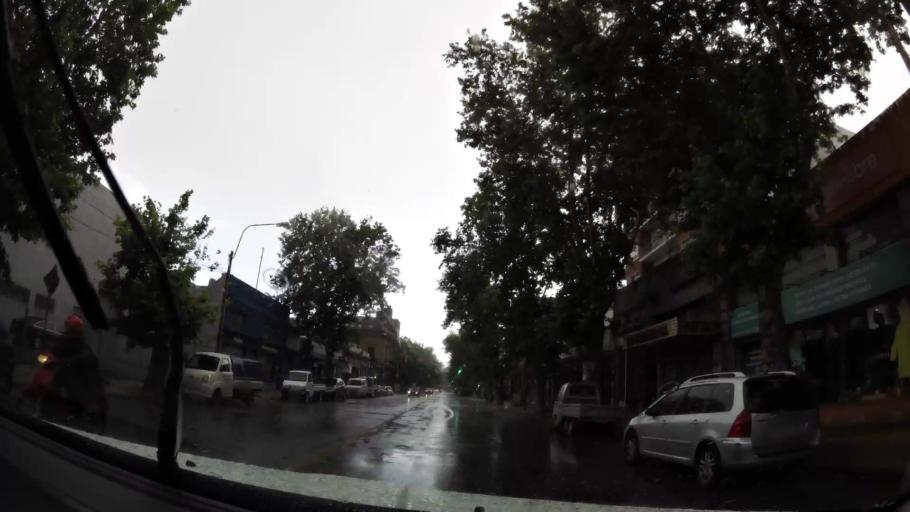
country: UY
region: Montevideo
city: Montevideo
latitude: -34.8856
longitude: -56.1844
